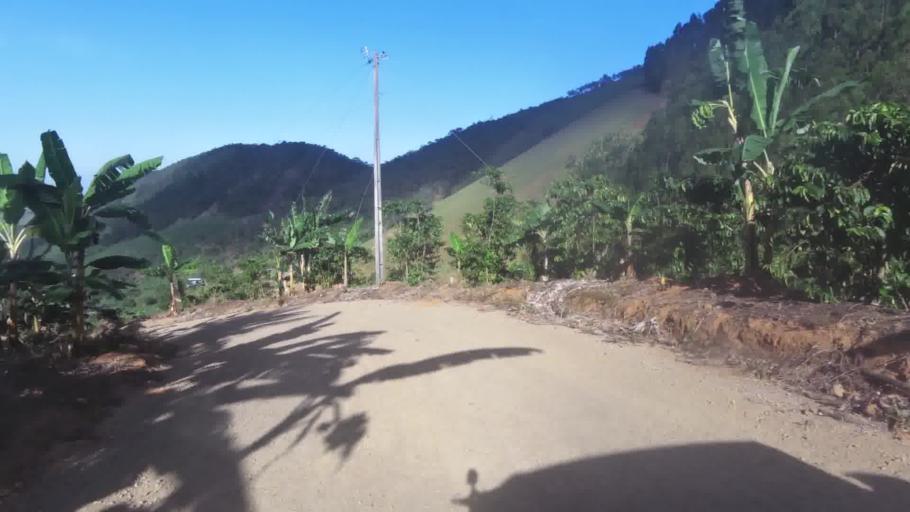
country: BR
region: Espirito Santo
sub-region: Iconha
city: Iconha
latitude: -20.7514
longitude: -40.8055
